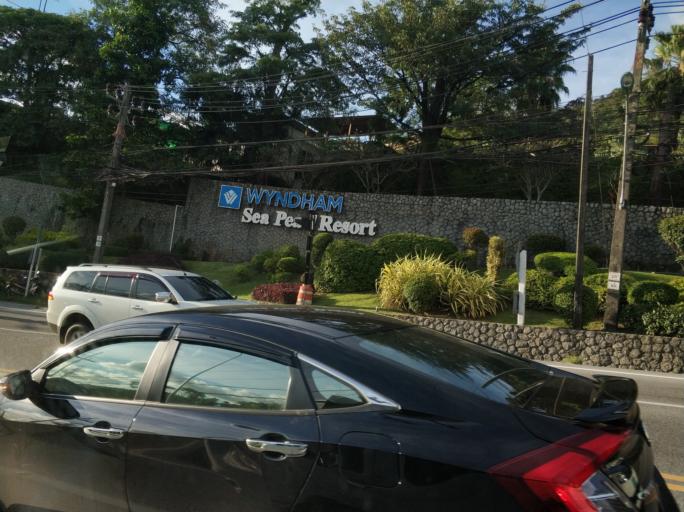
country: TH
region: Phuket
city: Patong
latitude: 7.9038
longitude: 98.3130
